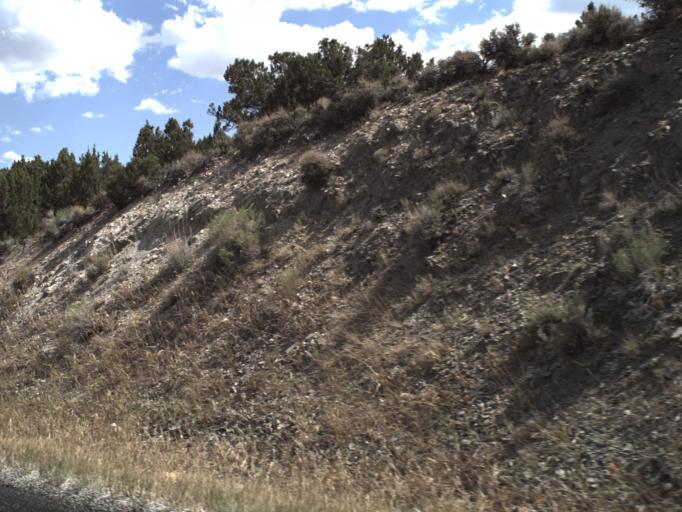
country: US
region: Idaho
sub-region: Minidoka County
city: Rupert
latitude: 41.9802
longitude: -113.1669
